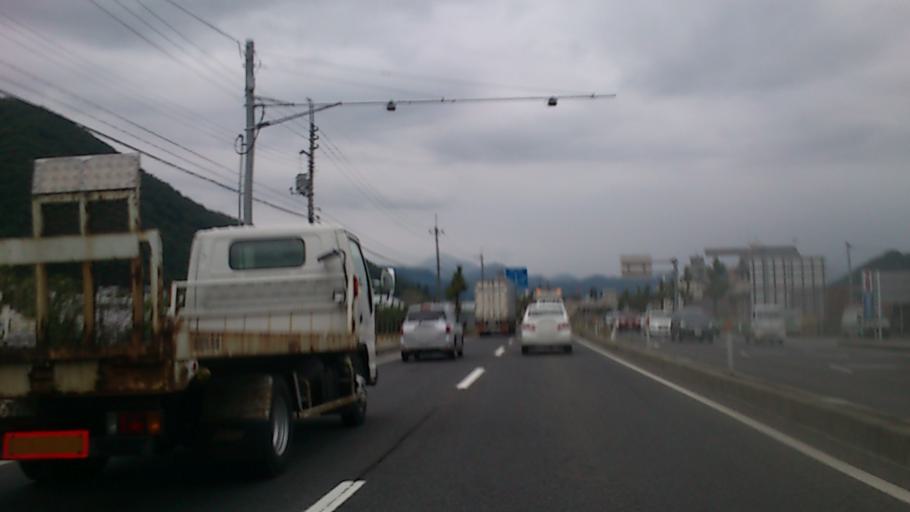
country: JP
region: Yamagata
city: Tendo
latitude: 38.3644
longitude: 140.3870
